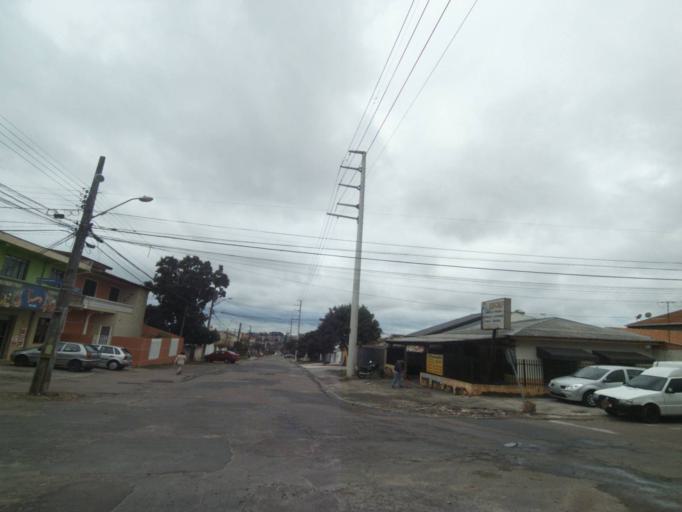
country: BR
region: Parana
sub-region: Curitiba
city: Curitiba
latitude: -25.5180
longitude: -49.3061
